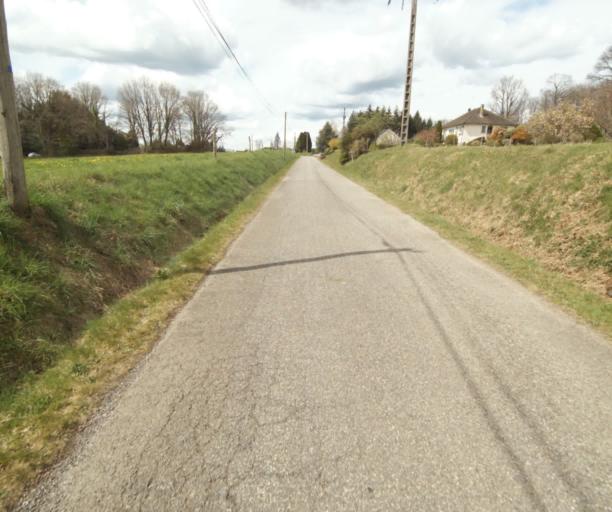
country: FR
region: Limousin
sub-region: Departement de la Correze
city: Laguenne
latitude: 45.2280
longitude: 1.8784
